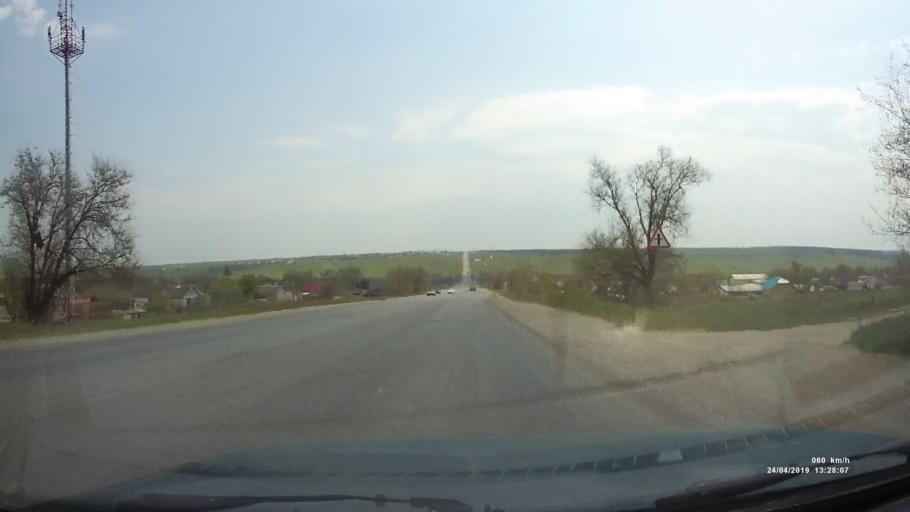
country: RU
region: Kalmykiya
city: Arshan'
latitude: 46.2751
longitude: 44.2283
